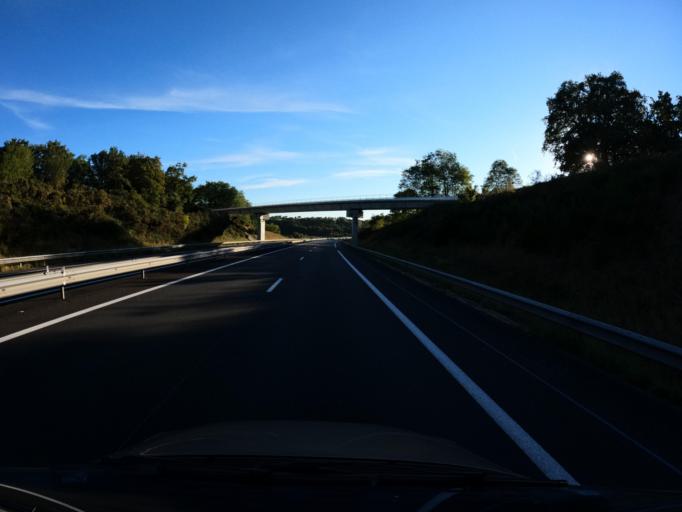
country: FR
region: Pays de la Loire
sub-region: Departement de la Vendee
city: Saint-Laurent-sur-Sevre
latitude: 46.9700
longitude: -0.9186
